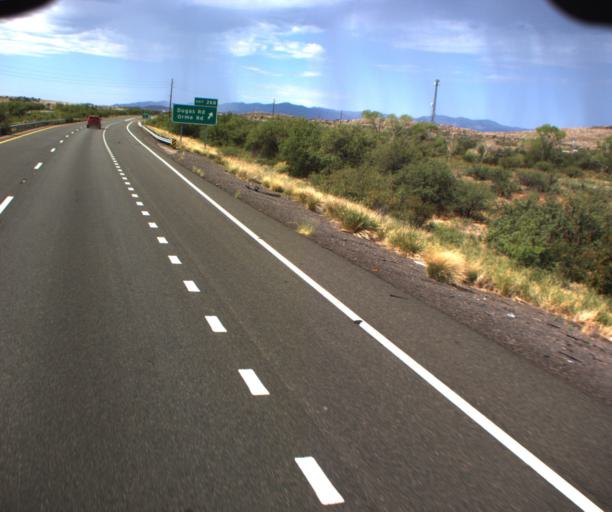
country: US
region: Arizona
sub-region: Yavapai County
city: Cordes Lakes
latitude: 34.4082
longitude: -112.0713
